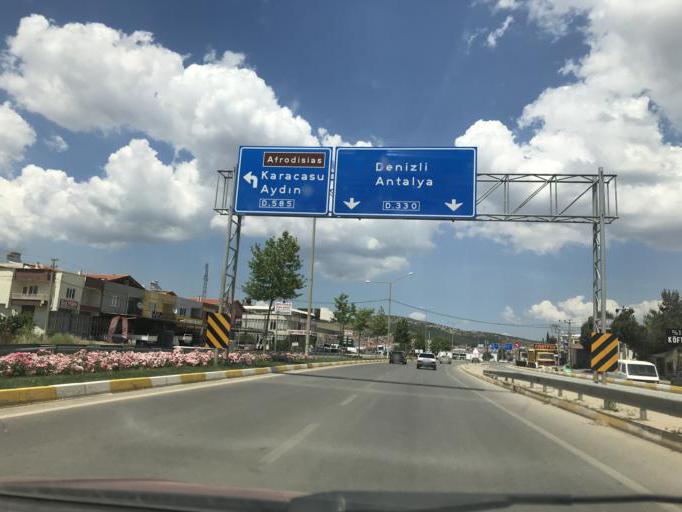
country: TR
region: Denizli
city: Tavas
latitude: 37.5623
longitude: 29.0615
